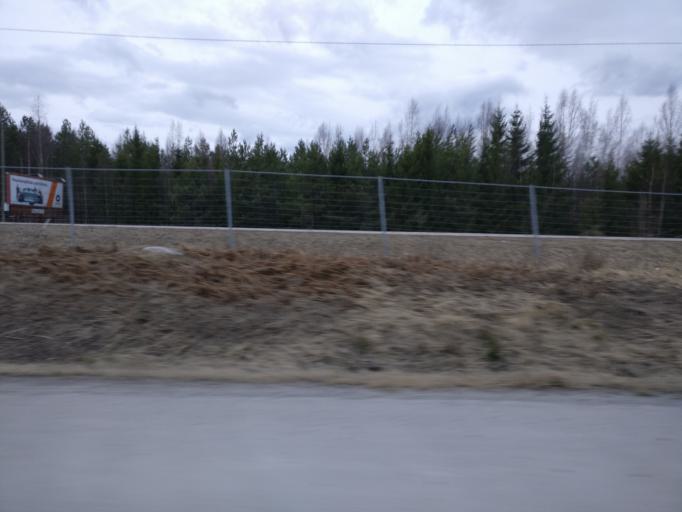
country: FI
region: Uusimaa
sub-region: Helsinki
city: Nurmijaervi
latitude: 60.4937
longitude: 24.8512
